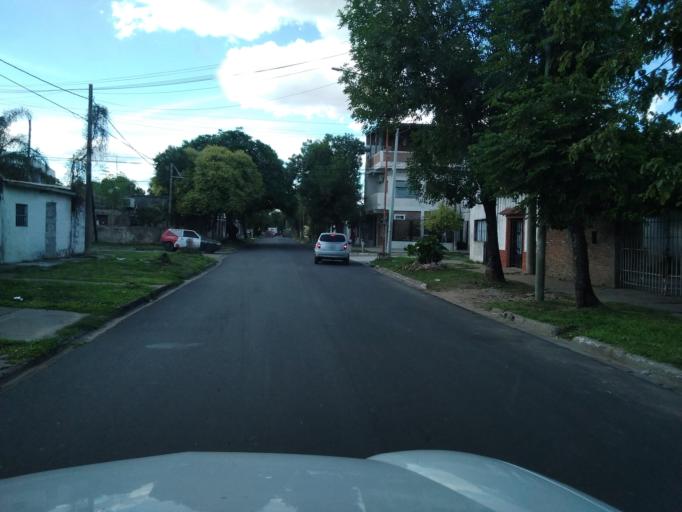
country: AR
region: Corrientes
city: Corrientes
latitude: -27.4822
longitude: -58.8373
